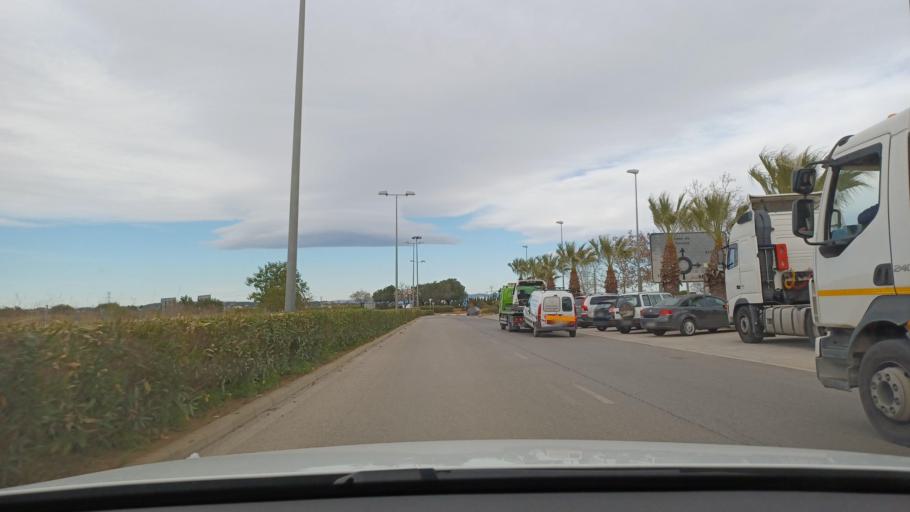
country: ES
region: Valencia
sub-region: Provincia de Valencia
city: Picassent
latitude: 39.3675
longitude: -0.4602
